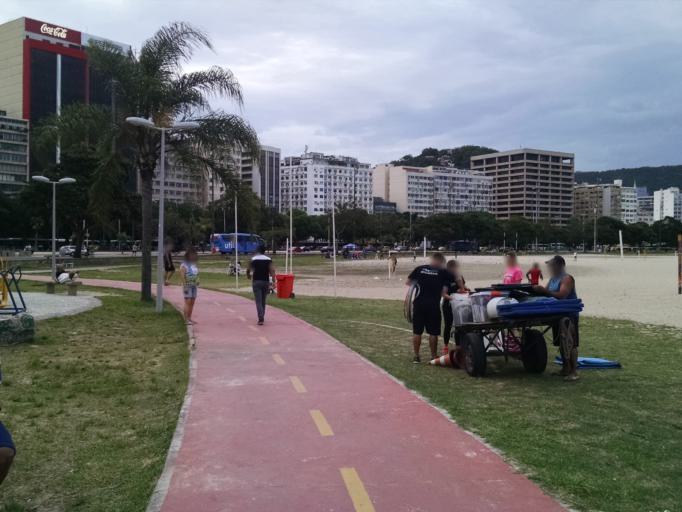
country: BR
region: Rio de Janeiro
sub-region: Rio De Janeiro
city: Rio de Janeiro
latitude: -22.9481
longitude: -43.1806
